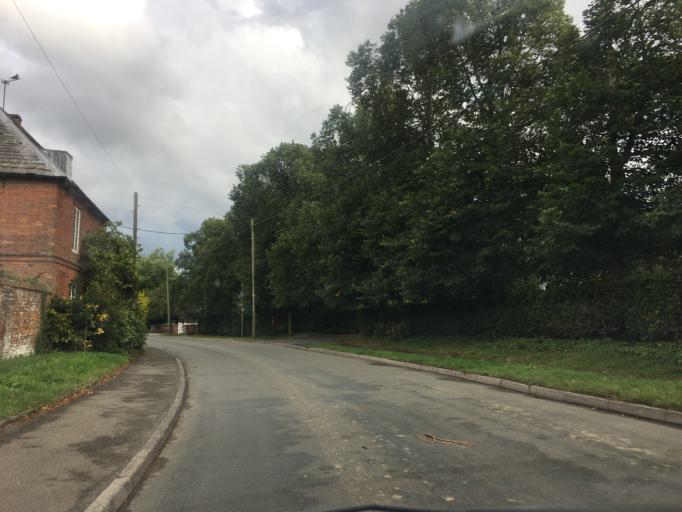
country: GB
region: England
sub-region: Leicestershire
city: Broughton Astley
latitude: 52.4910
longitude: -1.2247
